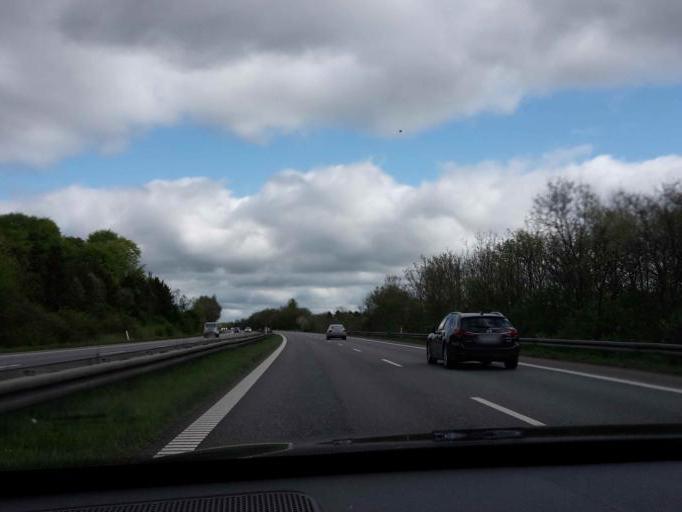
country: DK
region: Central Jutland
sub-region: Arhus Kommune
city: Logten
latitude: 56.2610
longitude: 10.3237
